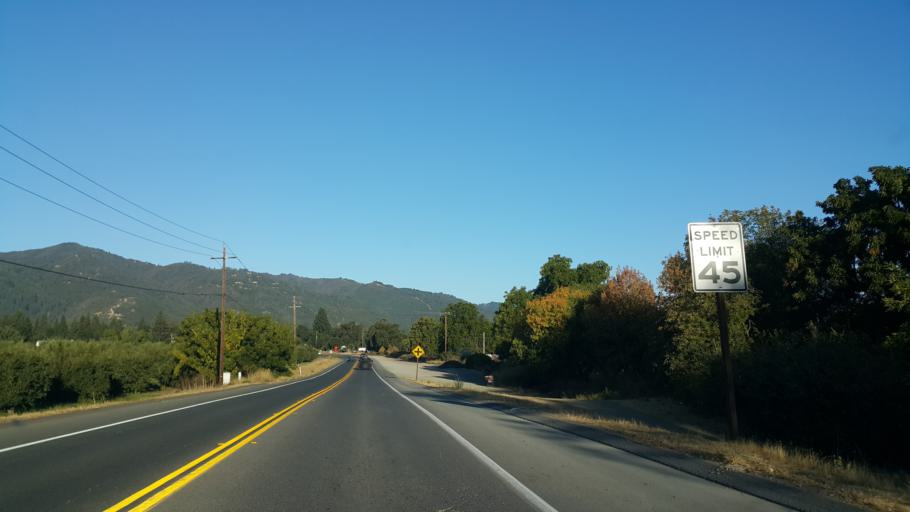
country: US
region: California
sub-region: Mendocino County
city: Talmage
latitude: 39.1350
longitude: -123.1881
